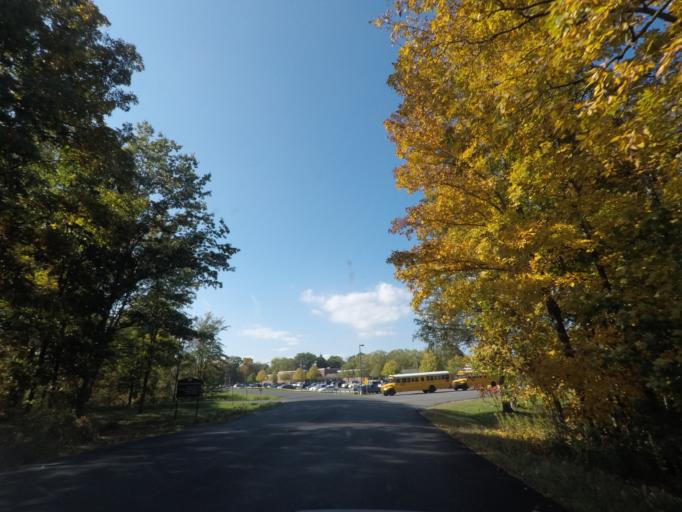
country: US
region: New York
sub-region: Rensselaer County
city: Averill Park
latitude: 42.6438
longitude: -73.5706
